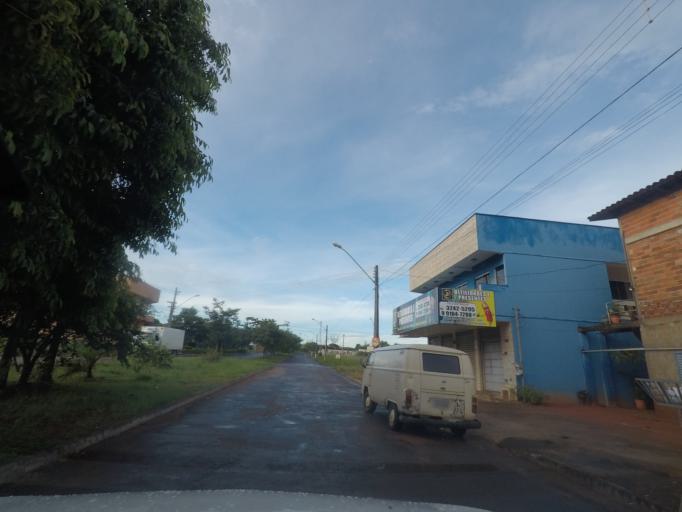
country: BR
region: Goias
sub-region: Goiania
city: Goiania
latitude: -16.7448
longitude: -49.3727
